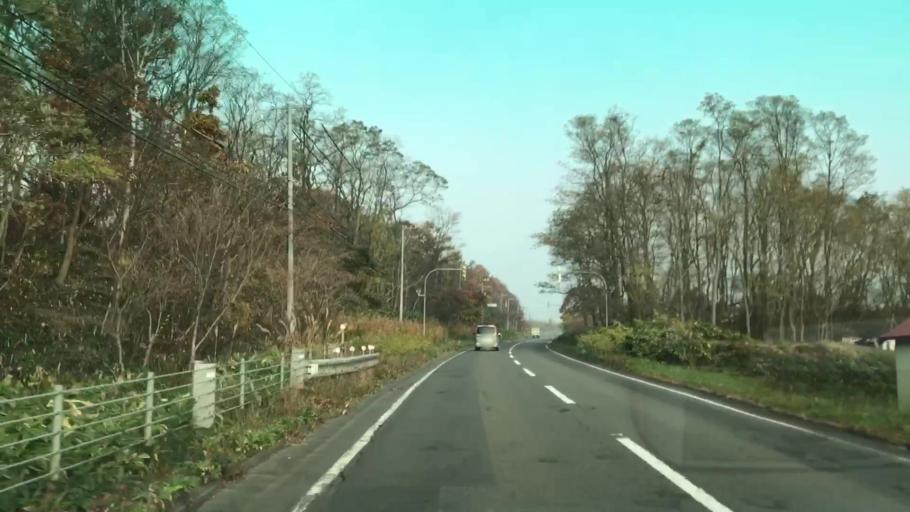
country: JP
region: Hokkaido
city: Ishikari
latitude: 43.3262
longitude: 141.4427
